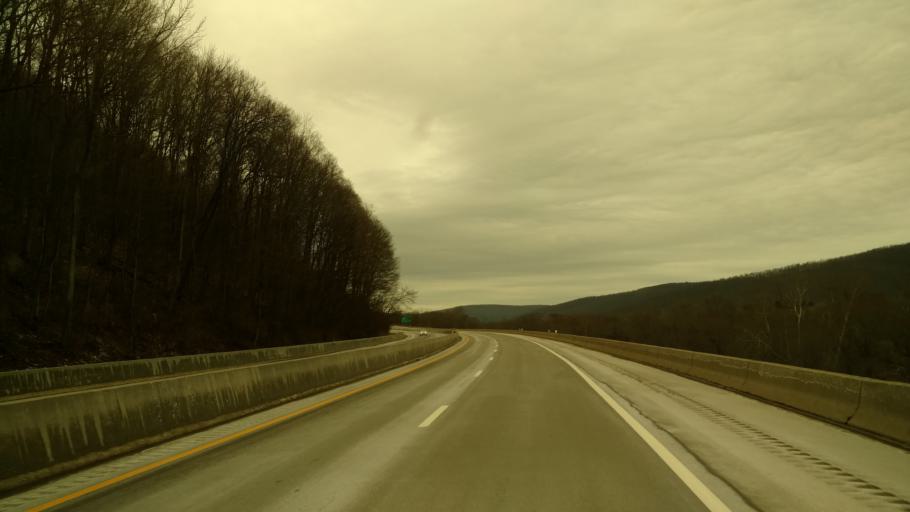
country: US
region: New York
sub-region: Cattaraugus County
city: Salamanca
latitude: 42.1505
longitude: -78.6916
